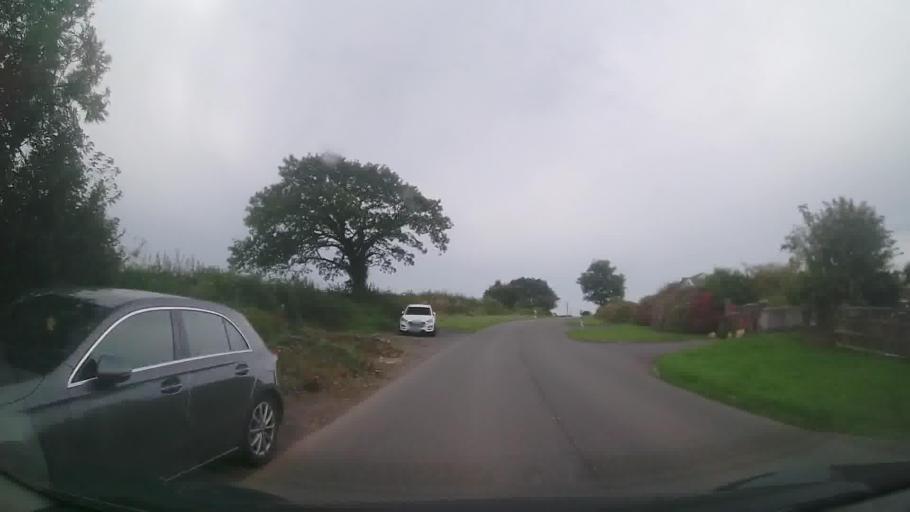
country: GB
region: Wales
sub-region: Pembrokeshire
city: Templeton
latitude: 51.7670
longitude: -4.7388
